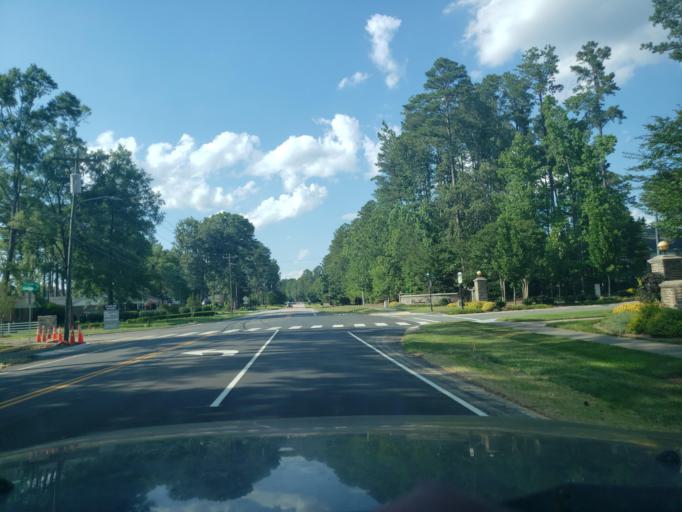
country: US
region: North Carolina
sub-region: Orange County
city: Chapel Hill
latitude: 35.9781
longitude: -78.9901
